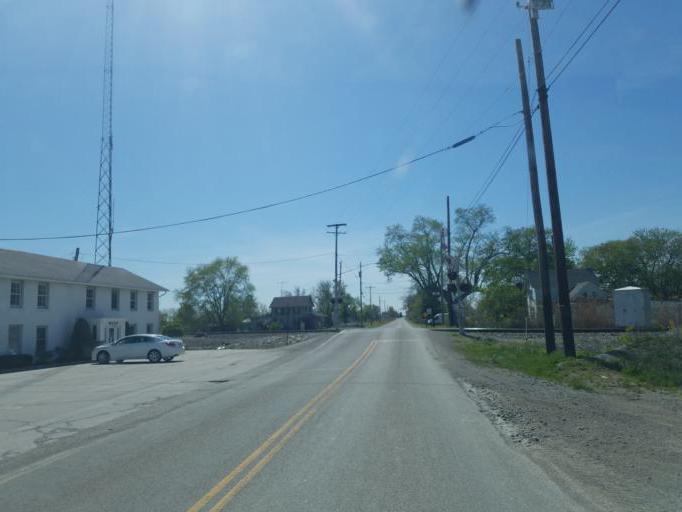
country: US
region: Ohio
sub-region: Huron County
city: Bellevue
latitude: 41.3438
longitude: -82.7867
